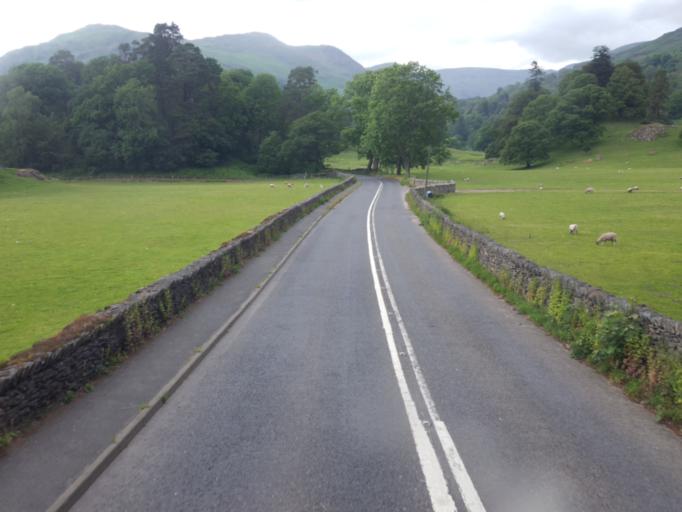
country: GB
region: England
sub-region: Cumbria
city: Ambleside
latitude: 54.4394
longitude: -2.9720
